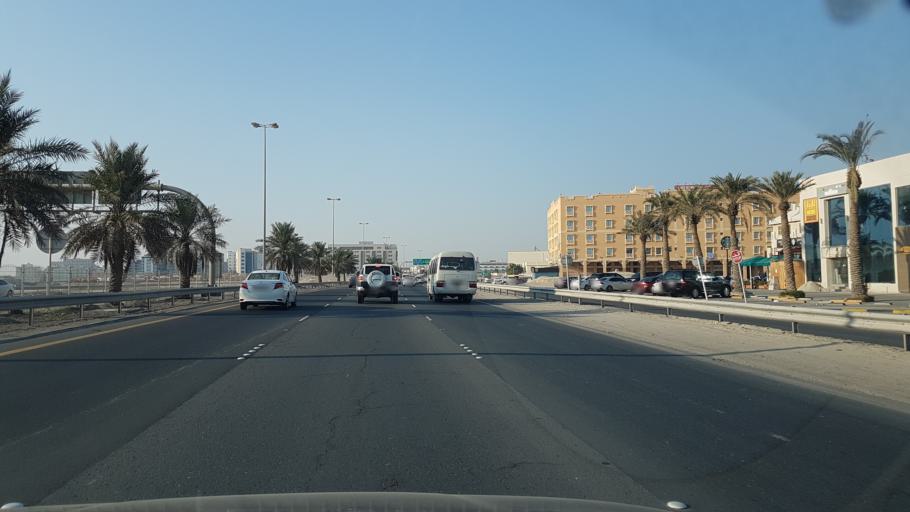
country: BH
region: Northern
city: Ar Rifa'
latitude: 26.1440
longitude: 50.5784
